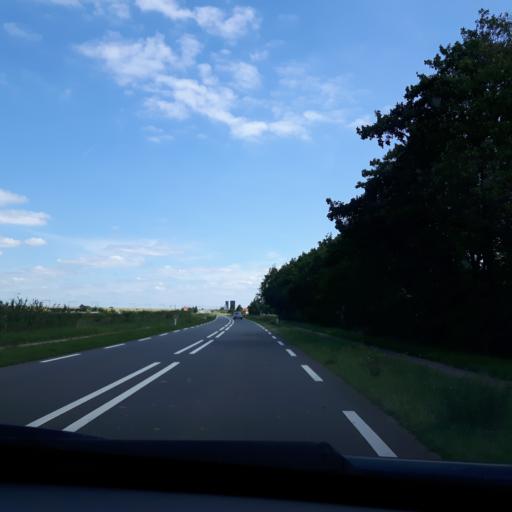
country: NL
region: Zeeland
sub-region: Gemeente Reimerswaal
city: Yerseke
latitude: 51.4669
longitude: 3.9815
